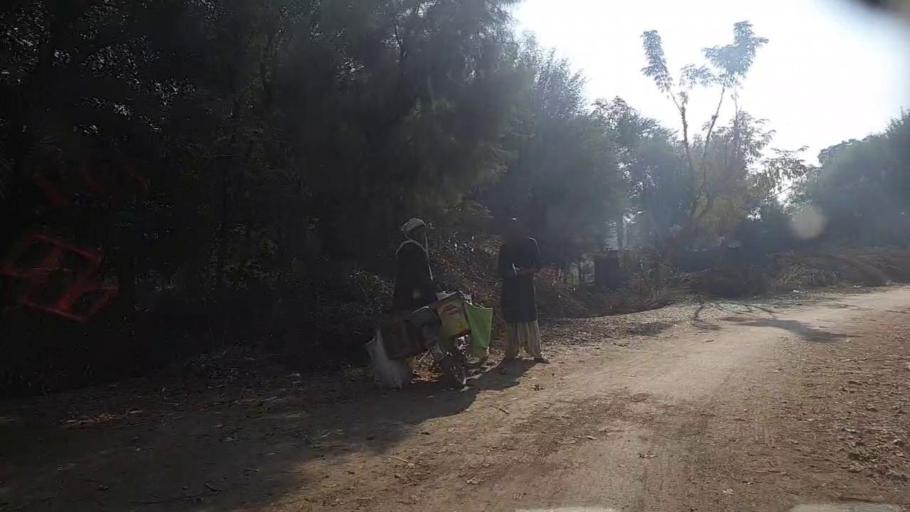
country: PK
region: Sindh
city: Kandiari
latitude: 27.0246
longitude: 68.5068
